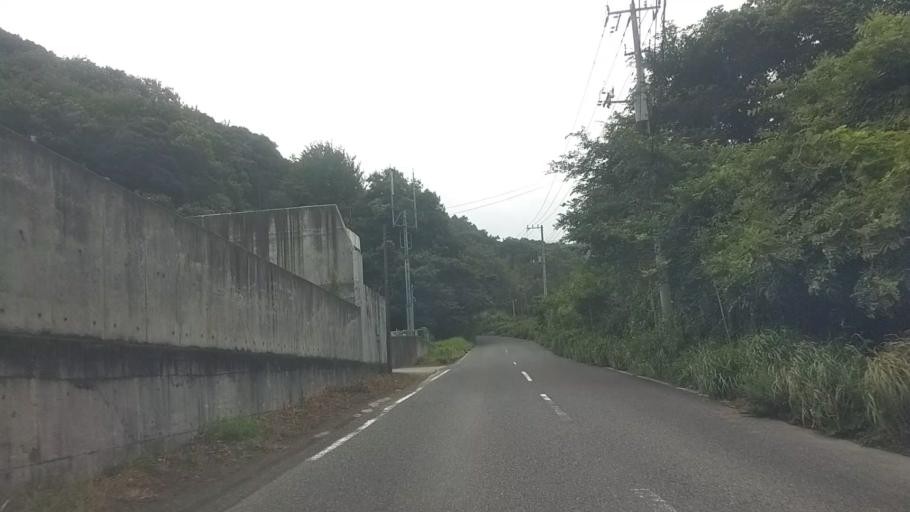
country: JP
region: Chiba
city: Kimitsu
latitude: 35.2382
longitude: 139.9870
